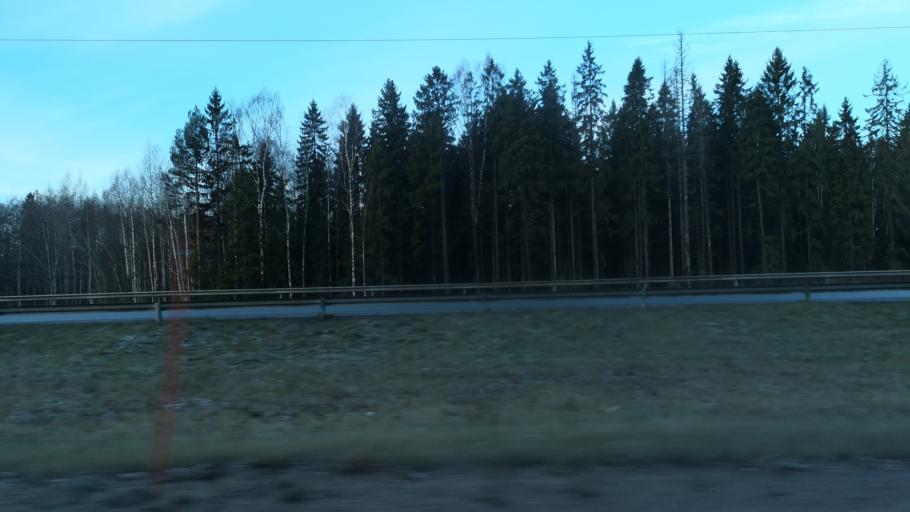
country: FI
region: Uusimaa
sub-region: Helsinki
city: Vantaa
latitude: 60.3144
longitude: 25.1072
